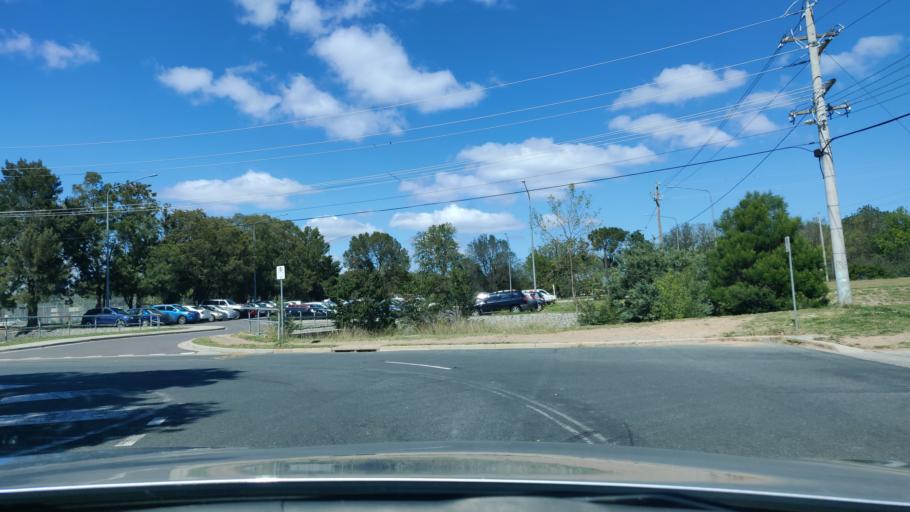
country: AU
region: Australian Capital Territory
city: Macarthur
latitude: -35.3666
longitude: 149.0939
